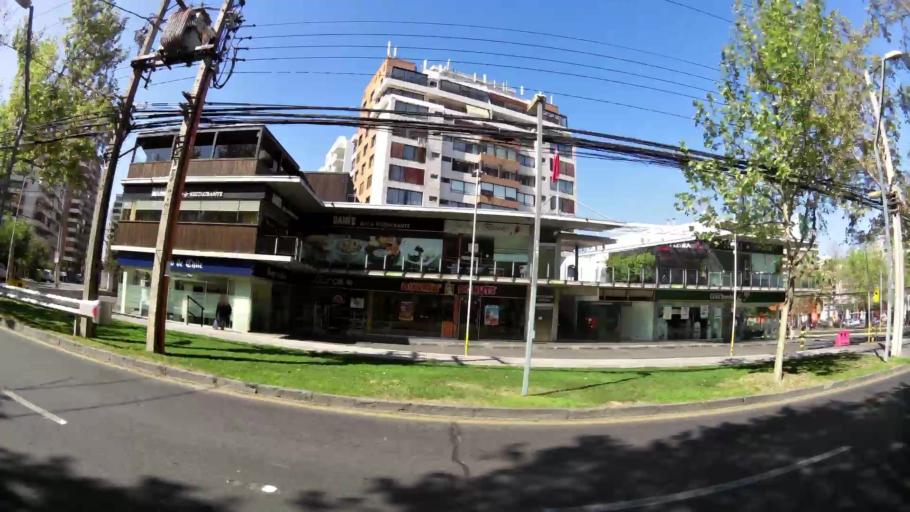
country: CL
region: Santiago Metropolitan
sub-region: Provincia de Santiago
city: Villa Presidente Frei, Nunoa, Santiago, Chile
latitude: -33.4234
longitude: -70.5784
